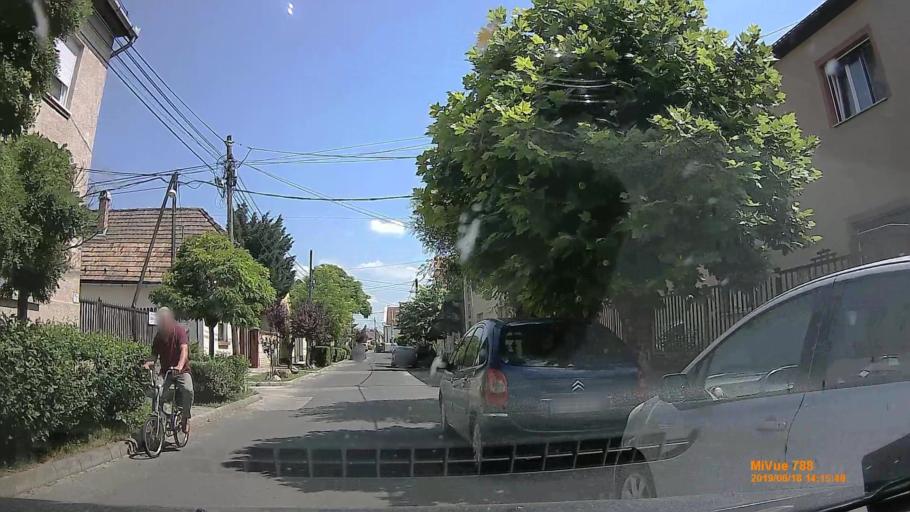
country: HU
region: Budapest
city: Budapest XXIII. keruelet
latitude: 47.3989
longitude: 19.1199
